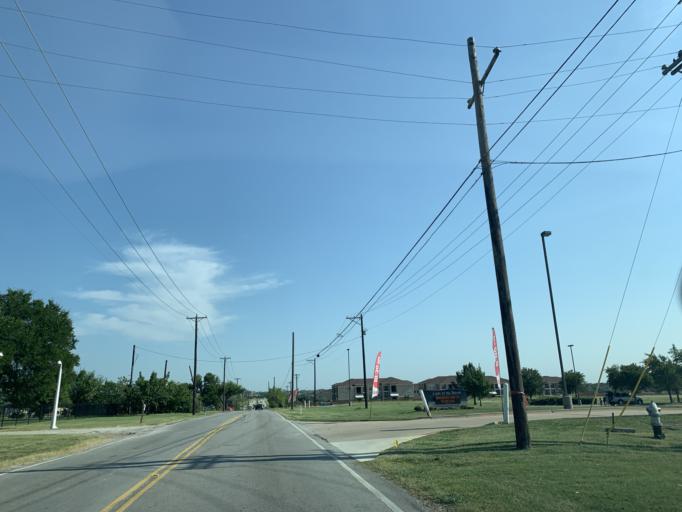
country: US
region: Texas
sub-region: Tarrant County
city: Blue Mound
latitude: 32.8981
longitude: -97.3069
